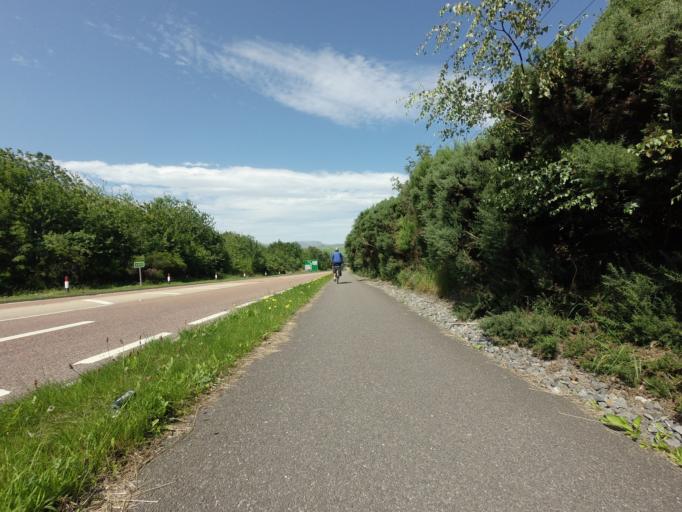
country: GB
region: Scotland
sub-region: Highland
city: Conon Bridge
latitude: 57.5672
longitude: -4.4245
